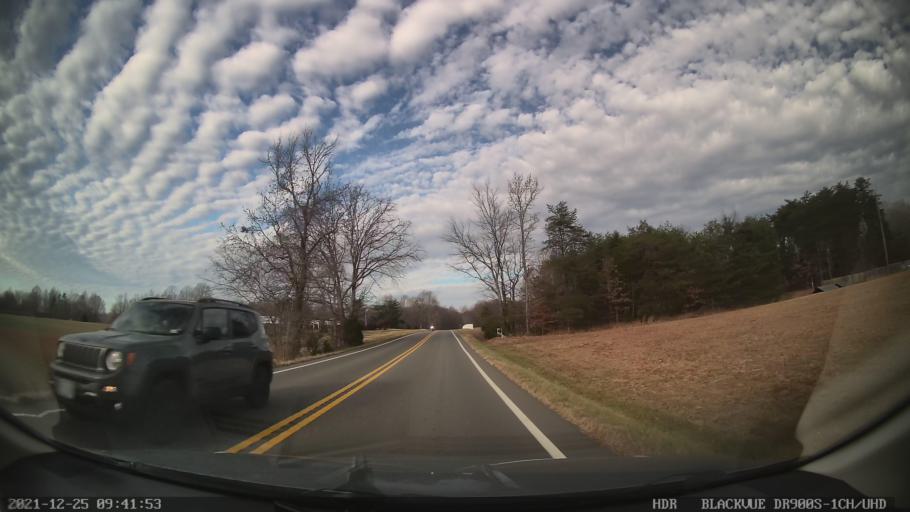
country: US
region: Virginia
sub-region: Goochland County
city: Goochland
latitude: 37.8198
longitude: -77.8827
